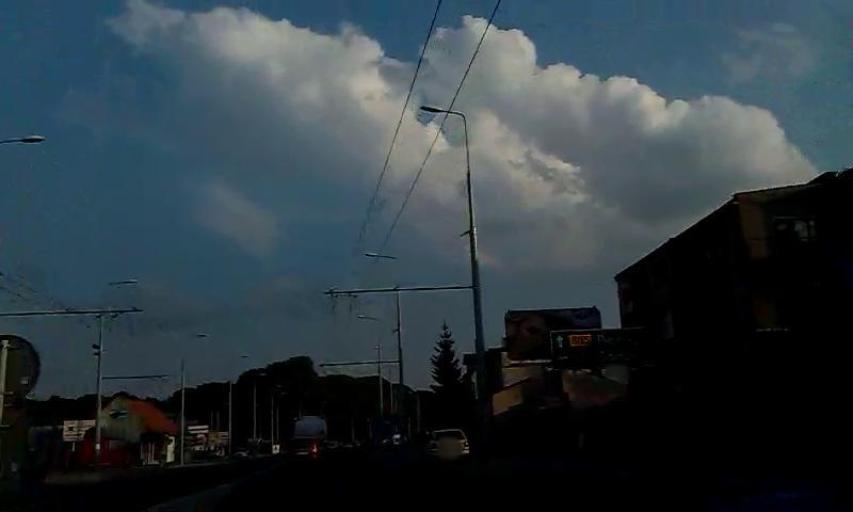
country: PL
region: Lublin Voivodeship
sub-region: Powiat lubelski
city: Lublin
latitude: 51.2093
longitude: 22.5856
